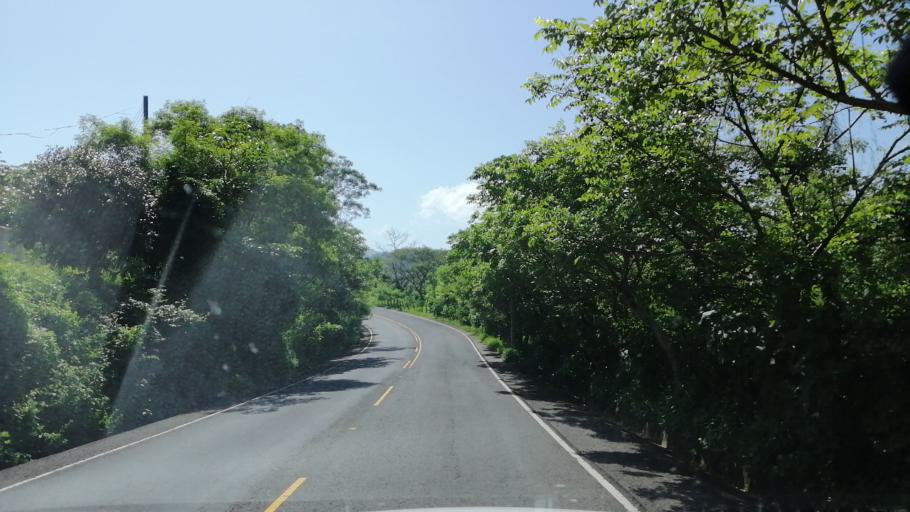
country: HN
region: Lempira
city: La Virtud
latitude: 13.9573
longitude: -88.7613
